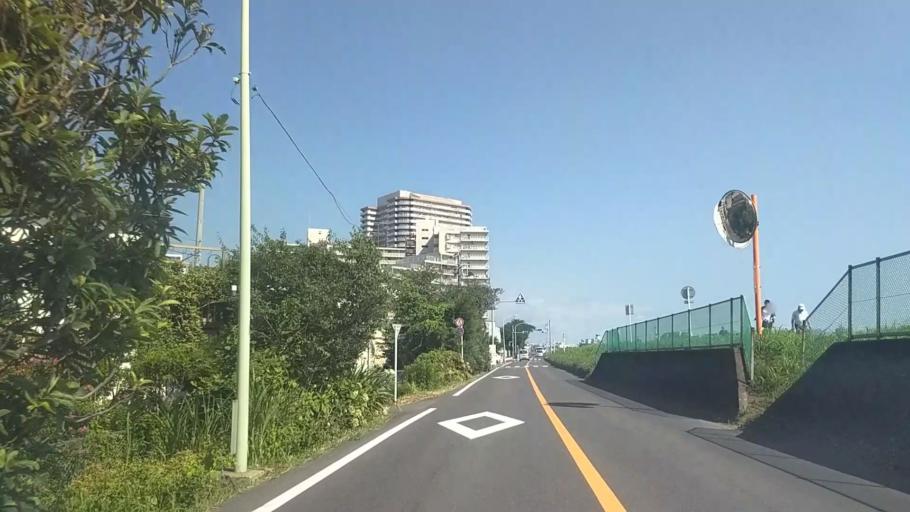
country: JP
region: Kanagawa
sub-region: Kawasaki-shi
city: Kawasaki
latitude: 35.5564
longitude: 139.7003
